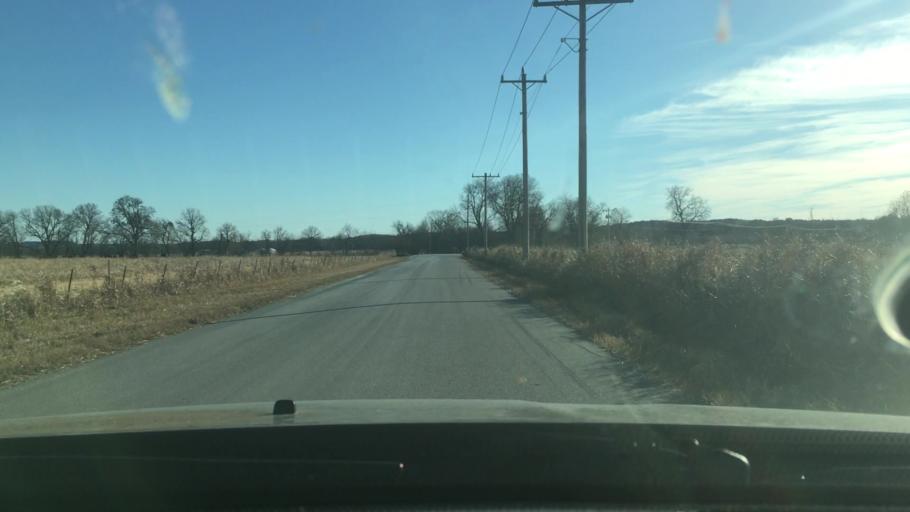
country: US
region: Oklahoma
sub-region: Murray County
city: Davis
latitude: 34.5011
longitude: -97.1559
